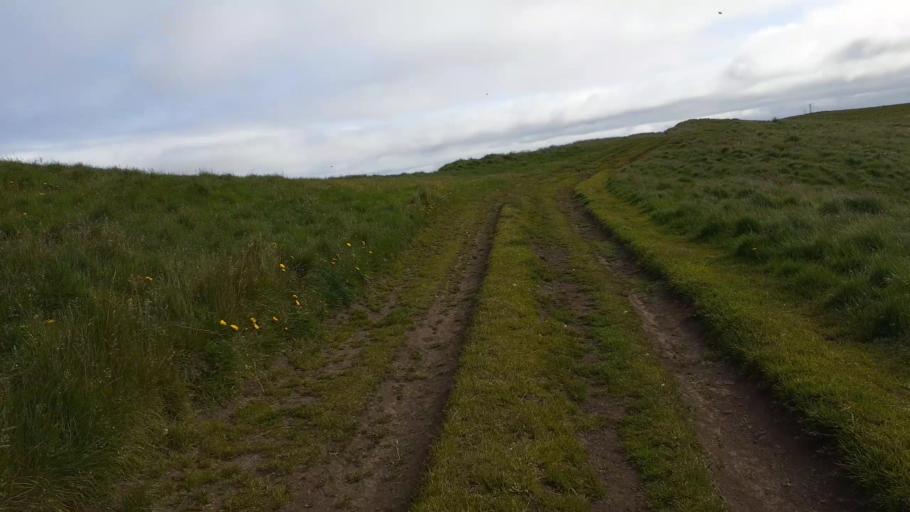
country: IS
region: Northeast
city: Dalvik
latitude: 66.5560
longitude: -18.0029
